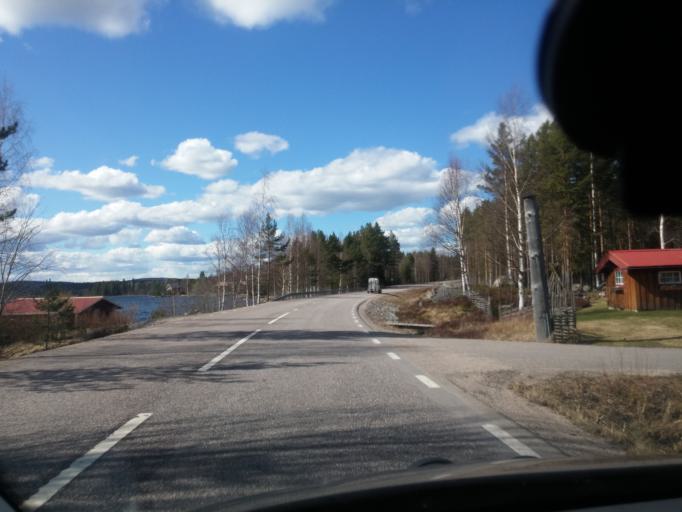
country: SE
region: Gaevleborg
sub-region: Ovanakers Kommun
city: Edsbyn
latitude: 61.2527
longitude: 15.8900
